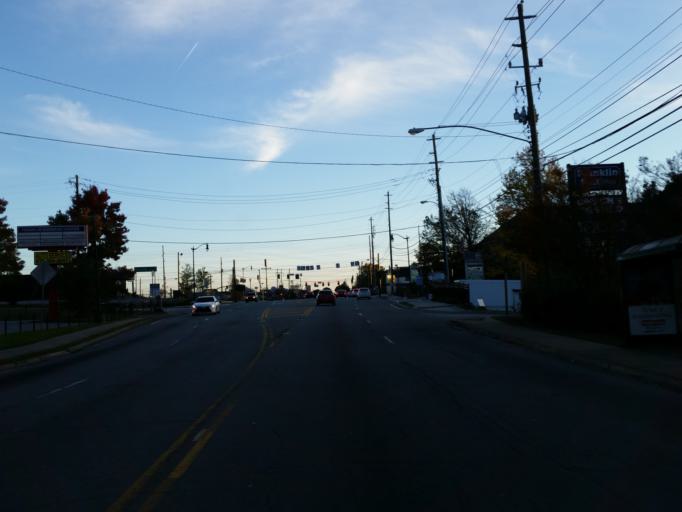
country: US
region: Georgia
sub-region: Cobb County
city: Smyrna
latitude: 33.9247
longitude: -84.4921
